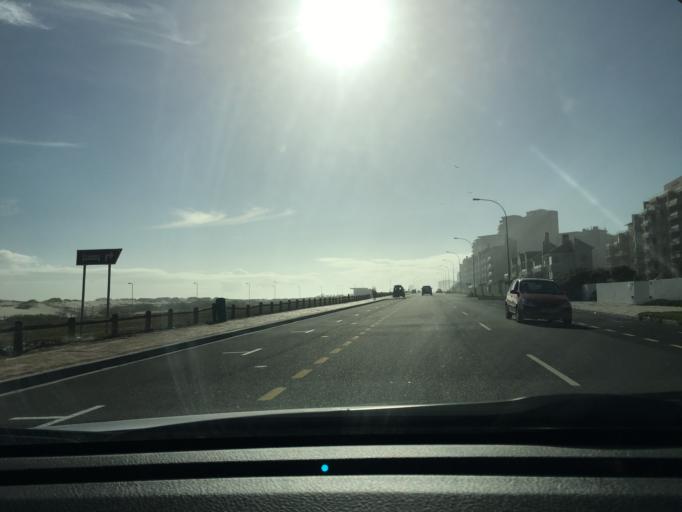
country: ZA
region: Western Cape
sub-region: City of Cape Town
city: Sunset Beach
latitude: -33.8265
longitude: 18.4797
